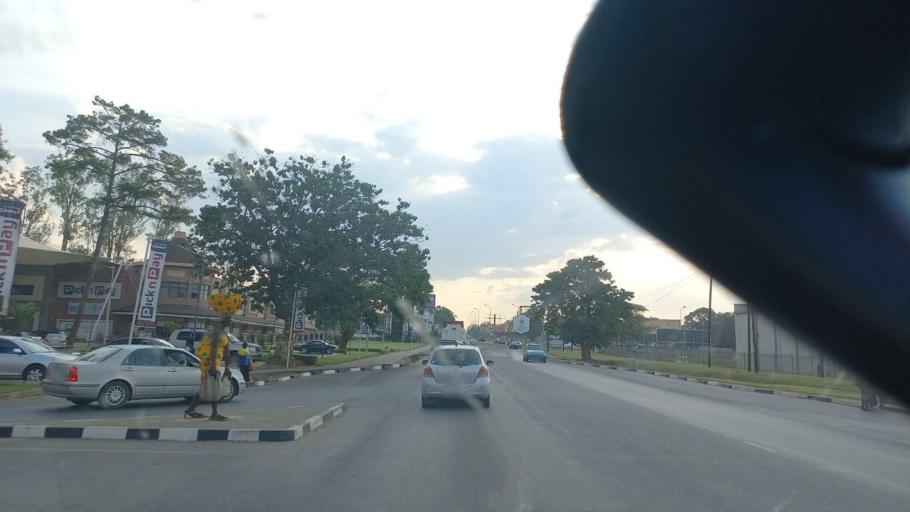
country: ZM
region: Lusaka
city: Lusaka
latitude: -15.3704
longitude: 28.4030
